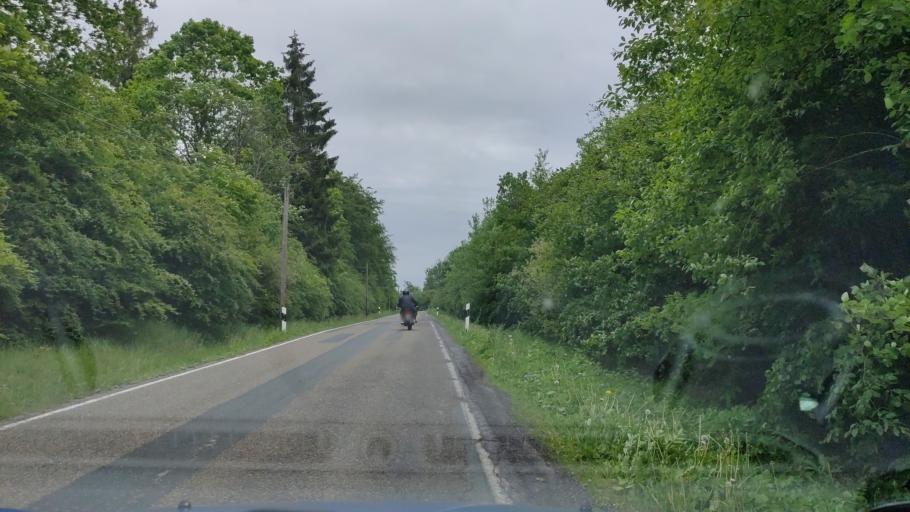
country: DE
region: Lower Saxony
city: Hardegsen
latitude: 51.7092
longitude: 9.7408
